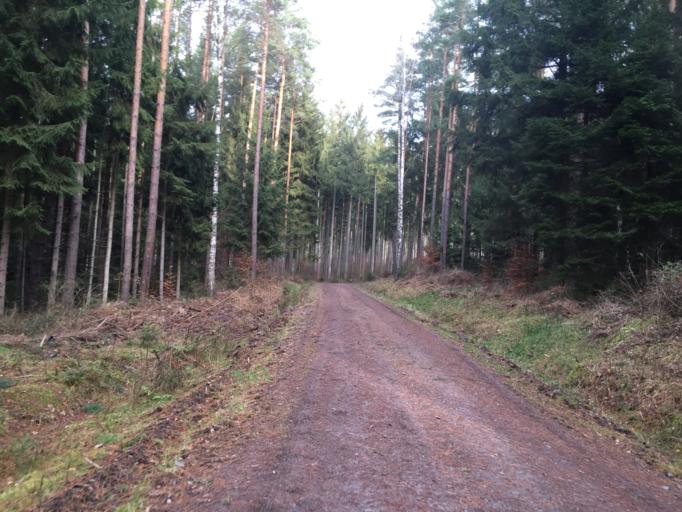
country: DE
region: Thuringia
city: Bollberg
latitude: 50.8884
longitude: 11.7854
